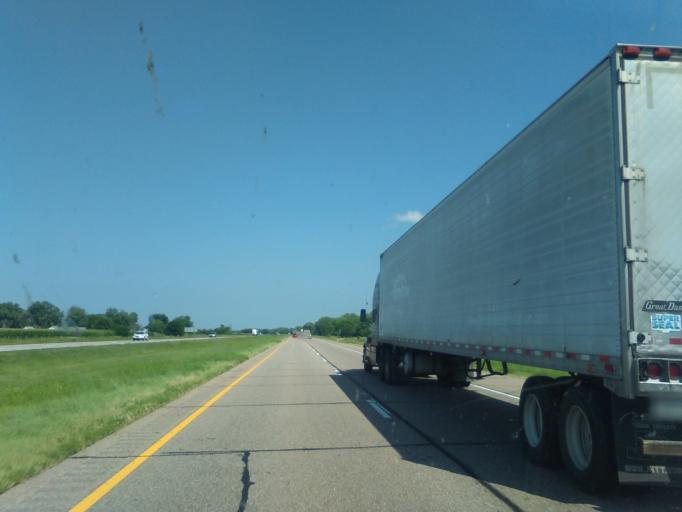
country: US
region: Nebraska
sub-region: Buffalo County
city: Kearney
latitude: 40.6736
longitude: -99.2328
